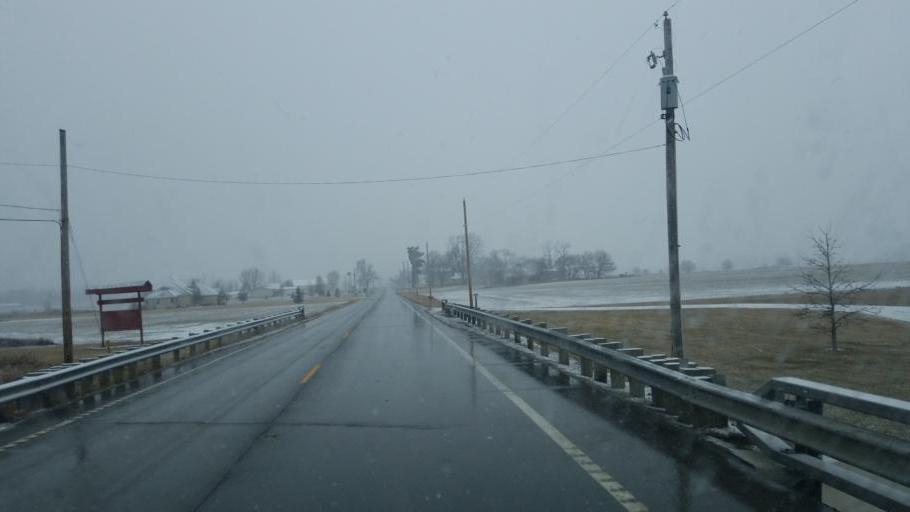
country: US
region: Ohio
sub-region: Defiance County
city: Hicksville
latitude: 41.3099
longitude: -84.7474
